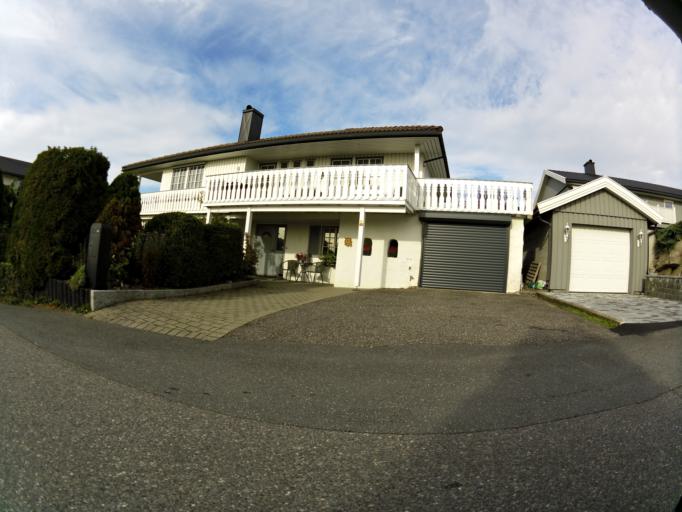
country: NO
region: Ostfold
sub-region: Fredrikstad
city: Fredrikstad
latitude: 59.2247
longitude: 10.9203
